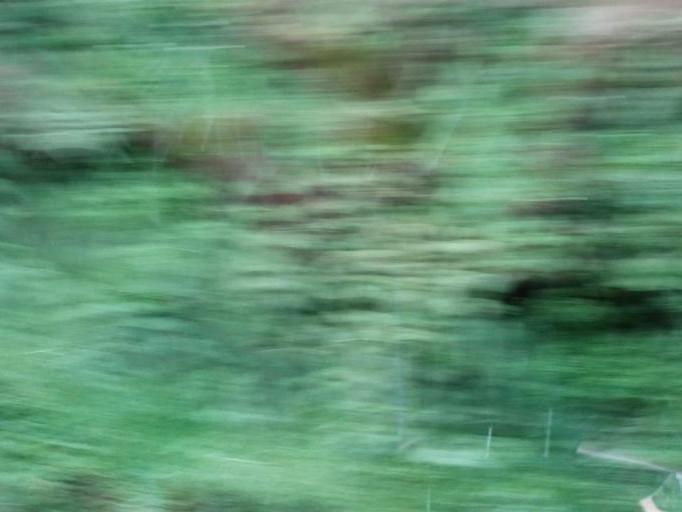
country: GT
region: Quetzaltenango
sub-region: Municipio de La Esperanza
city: La Esperanza
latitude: 14.8491
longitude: -91.5551
